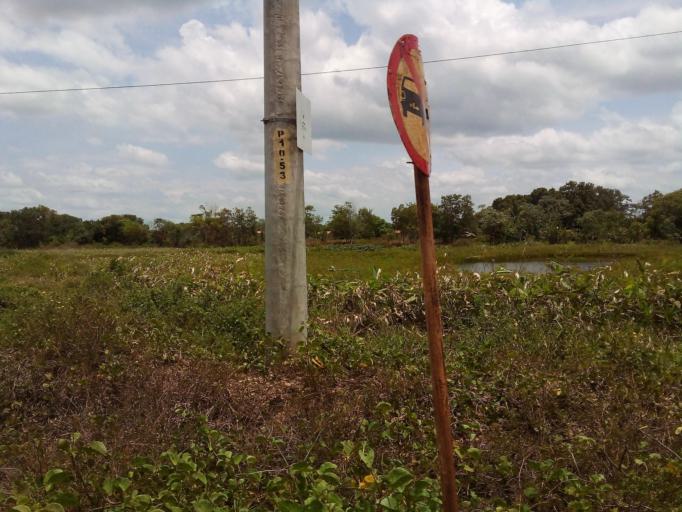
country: BR
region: Maranhao
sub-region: Itapecuru Mirim
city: Itapecuru Mirim
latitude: -3.0592
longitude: -44.3408
